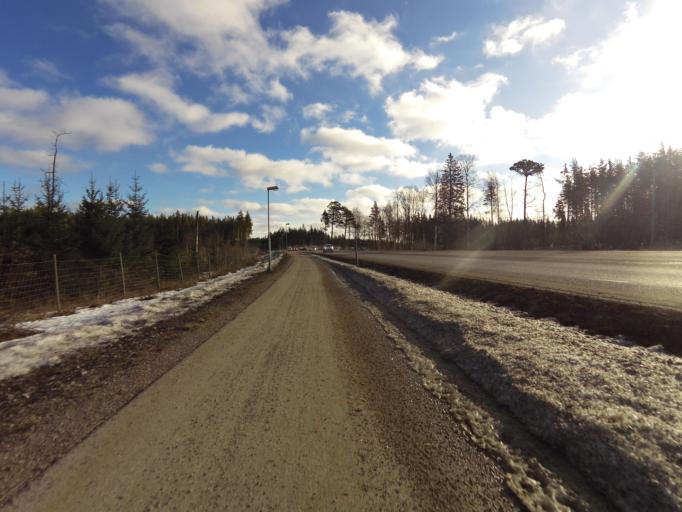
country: SE
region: Gaevleborg
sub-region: Gavle Kommun
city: Gavle
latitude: 60.6455
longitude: 17.2636
